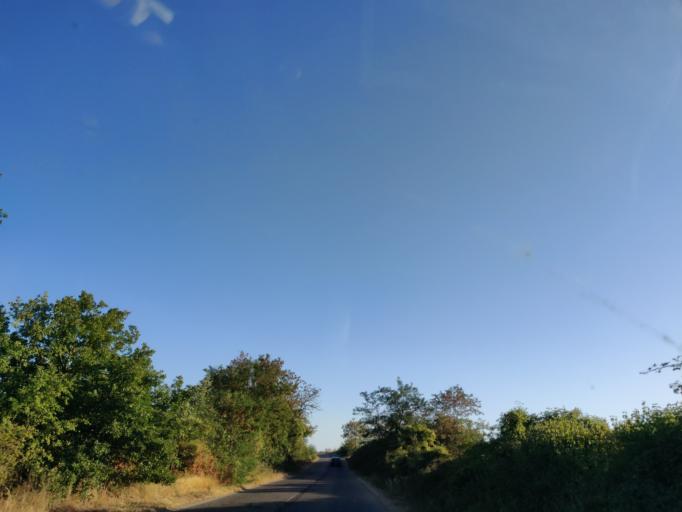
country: IT
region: Latium
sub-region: Provincia di Viterbo
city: Grotte di Castro
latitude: 42.6962
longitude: 11.8785
